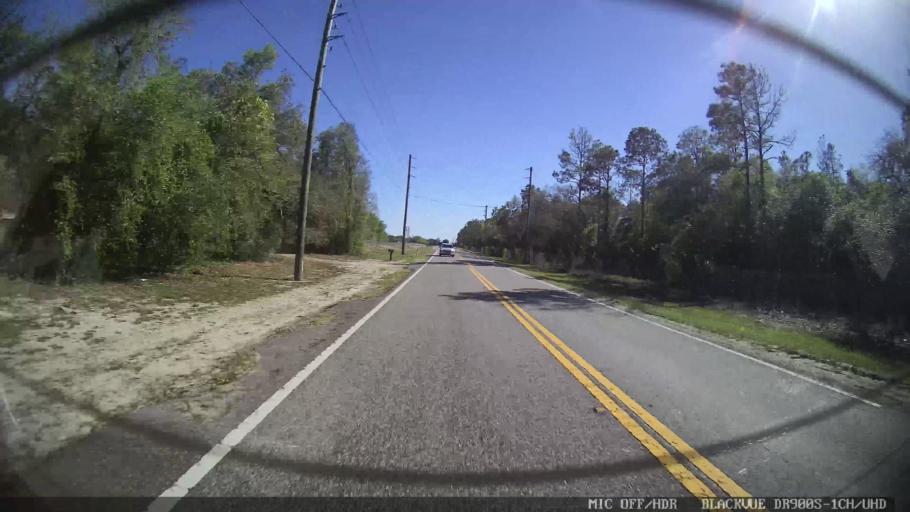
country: US
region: Florida
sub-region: Pasco County
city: Shady Hills
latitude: 28.3812
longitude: -82.5512
